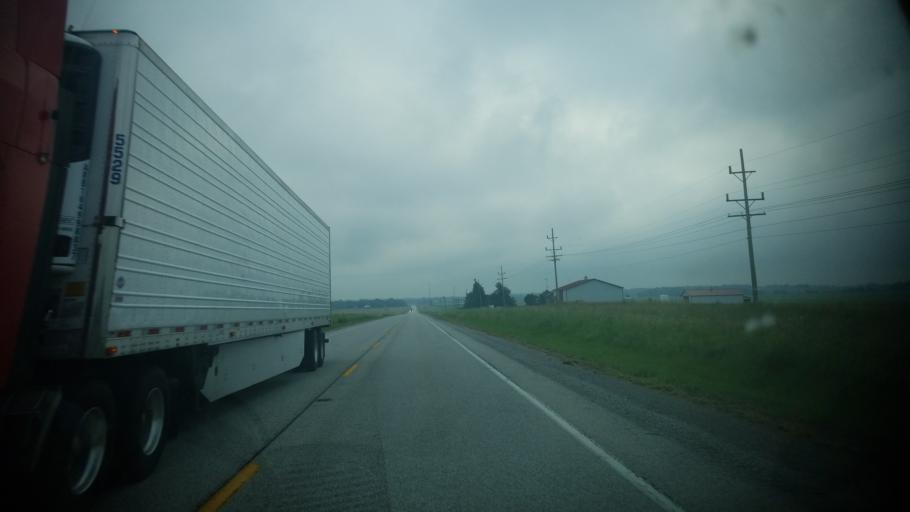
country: US
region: Illinois
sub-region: Clay County
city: Flora
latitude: 38.6775
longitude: -88.3901
